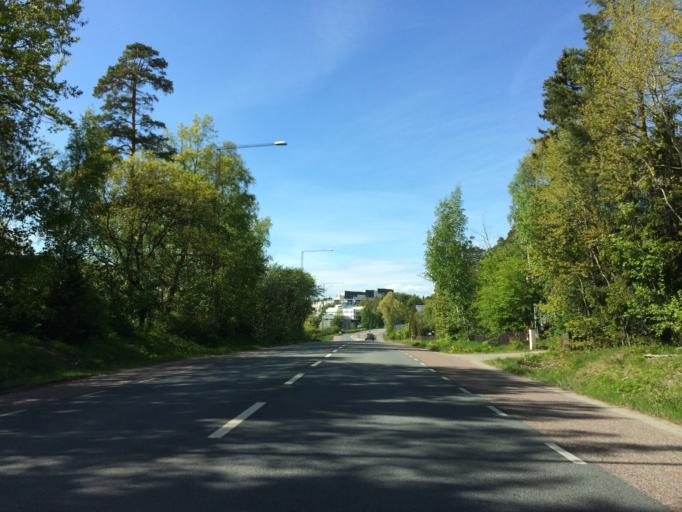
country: SE
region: Stockholm
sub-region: Sollentuna Kommun
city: Sollentuna
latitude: 59.4246
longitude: 18.0008
